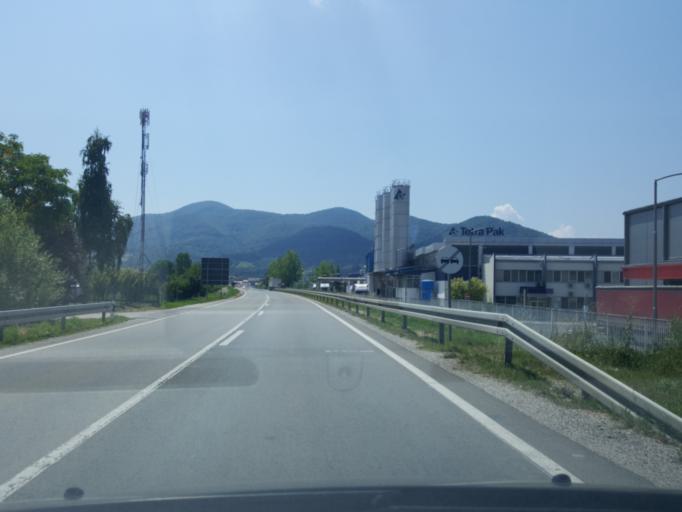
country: RS
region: Central Serbia
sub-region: Moravicki Okrug
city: Gornji Milanovac
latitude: 44.0173
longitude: 20.4636
